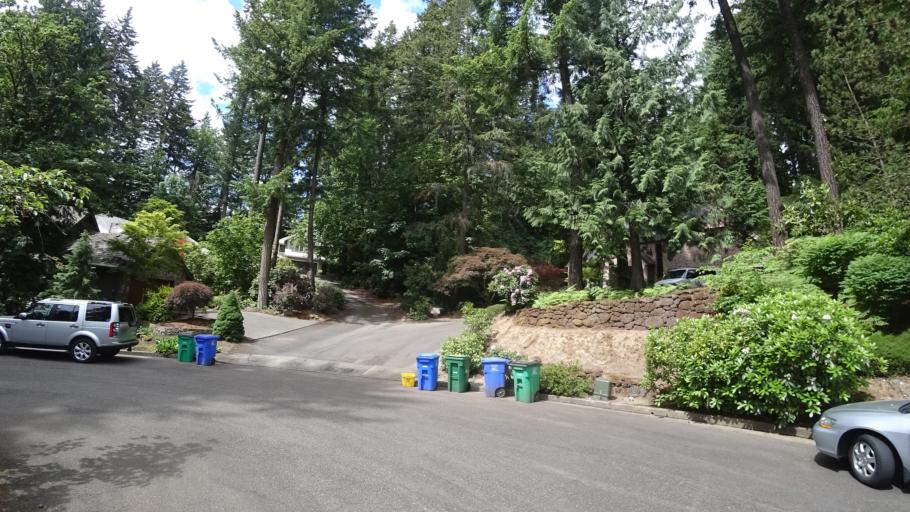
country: US
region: Oregon
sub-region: Clackamas County
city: Lake Oswego
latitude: 45.4468
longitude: -122.6946
